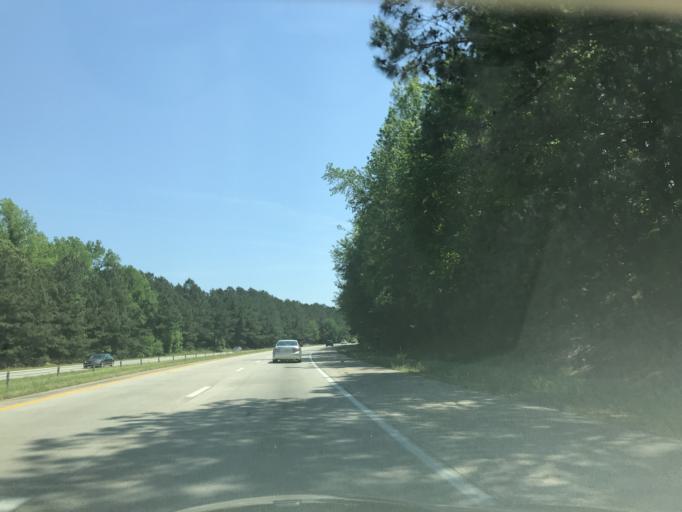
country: US
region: North Carolina
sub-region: Johnston County
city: Benson
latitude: 35.4535
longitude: -78.5347
